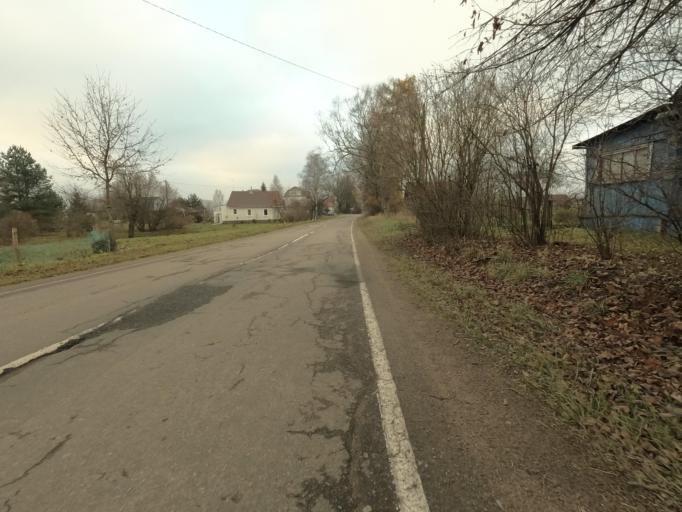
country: RU
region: Leningrad
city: Mga
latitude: 59.7832
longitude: 31.0241
